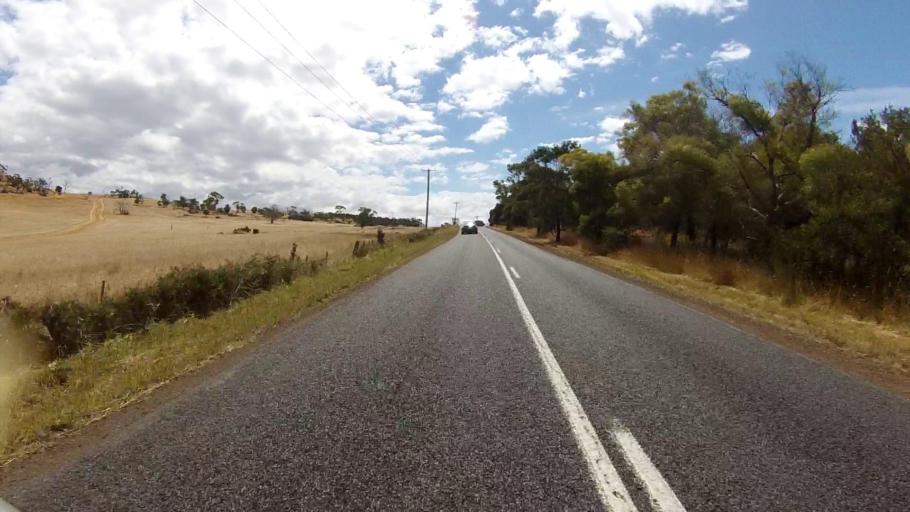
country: AU
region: Tasmania
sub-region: Sorell
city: Sorell
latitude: -42.1644
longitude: 148.0719
